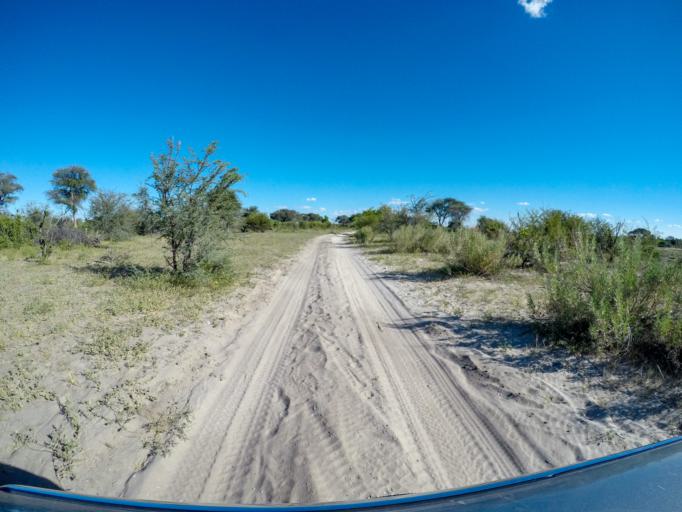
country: BW
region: Central
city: Rakops
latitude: -20.4643
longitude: 24.5202
